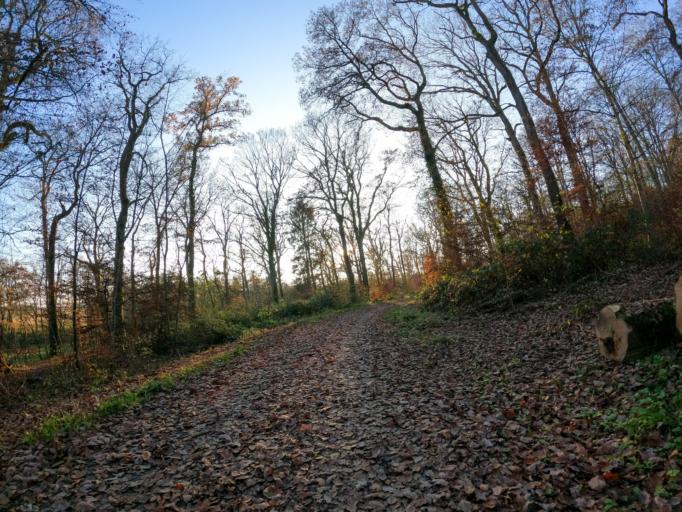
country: LU
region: Luxembourg
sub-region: Canton de Capellen
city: Mamer
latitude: 49.6083
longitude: 6.0177
